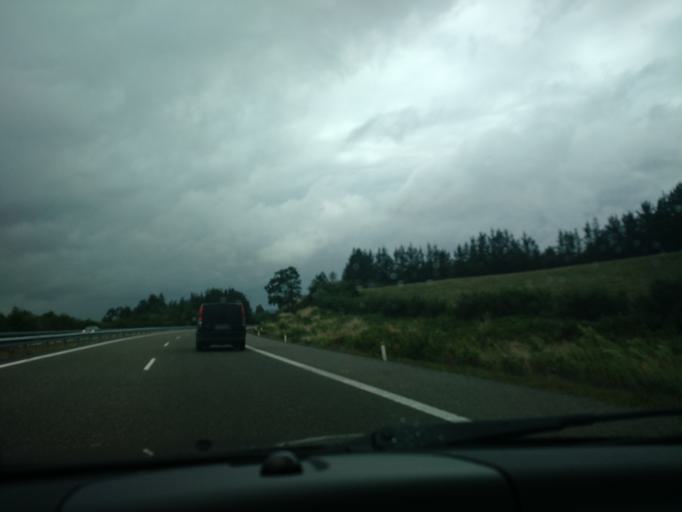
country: ES
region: Galicia
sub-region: Provincia da Coruna
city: Oroso
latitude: 42.9469
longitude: -8.4607
